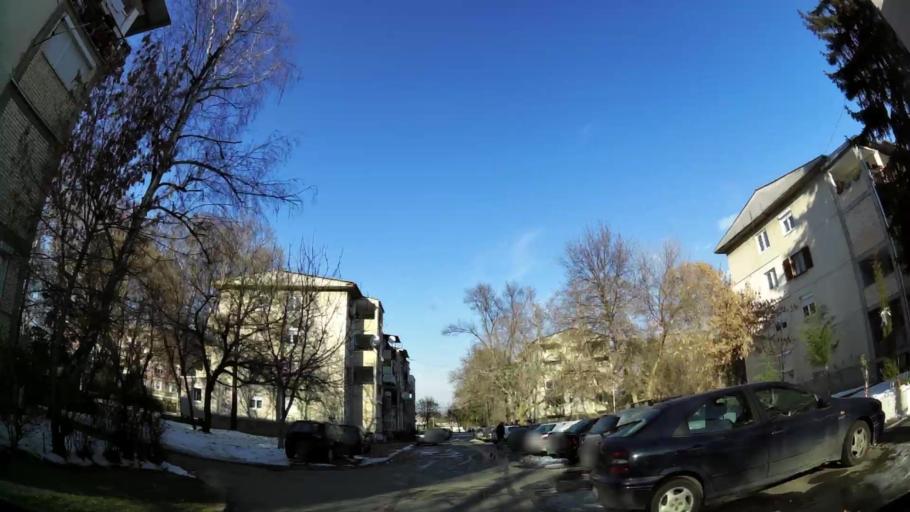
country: MK
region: Karpos
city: Skopje
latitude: 42.0065
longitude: 21.3945
